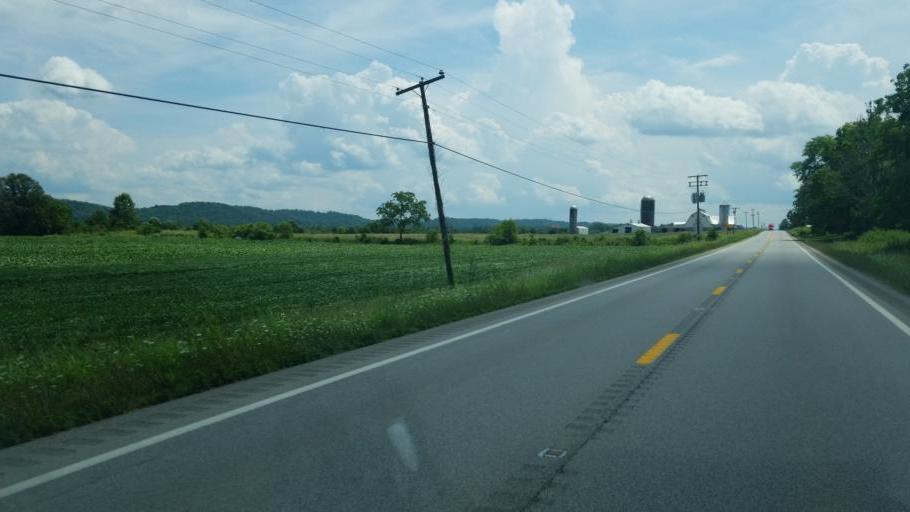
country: US
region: West Virginia
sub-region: Putnam County
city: Buffalo
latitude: 38.7308
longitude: -81.9732
